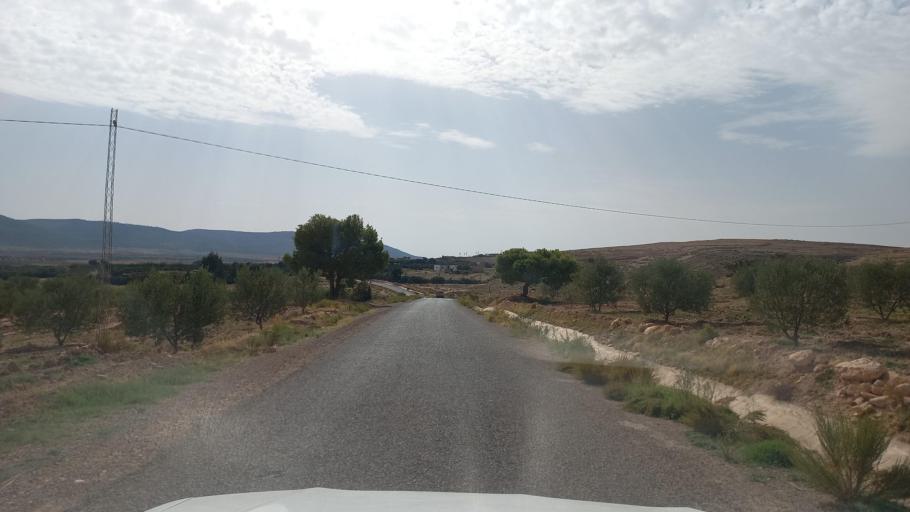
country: TN
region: Al Qasrayn
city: Kasserine
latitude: 35.3669
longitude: 8.8566
